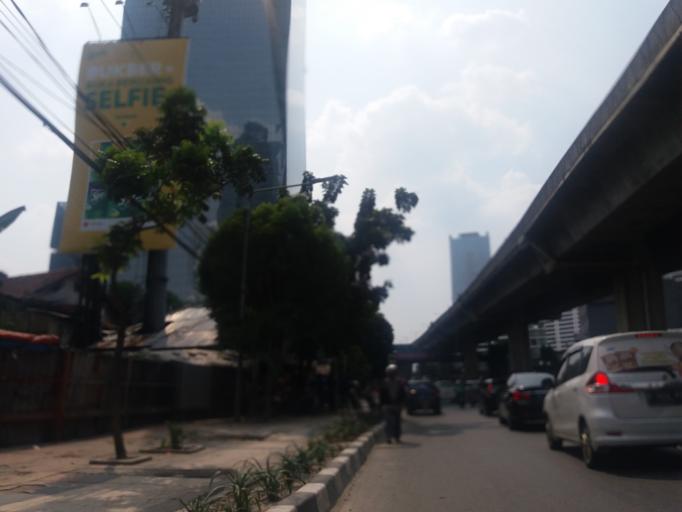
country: ID
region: Jakarta Raya
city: Jakarta
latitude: -6.2190
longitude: 106.8195
